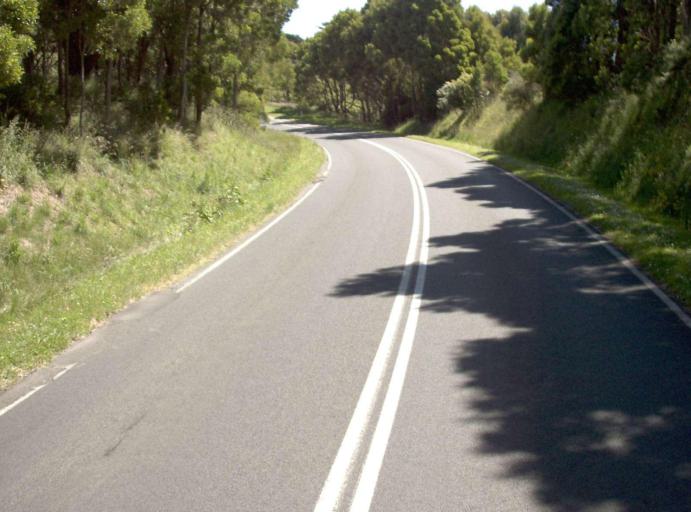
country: AU
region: Victoria
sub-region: Latrobe
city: Morwell
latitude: -38.6703
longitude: 146.1603
